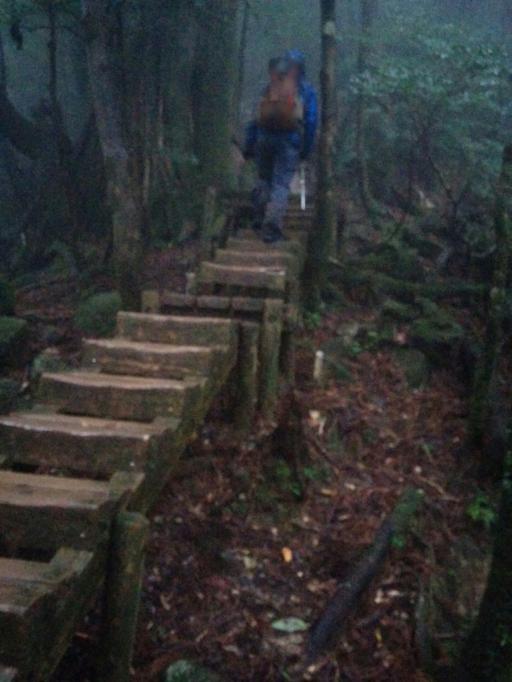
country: JP
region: Kagoshima
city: Nishinoomote
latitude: 30.3566
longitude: 130.5416
